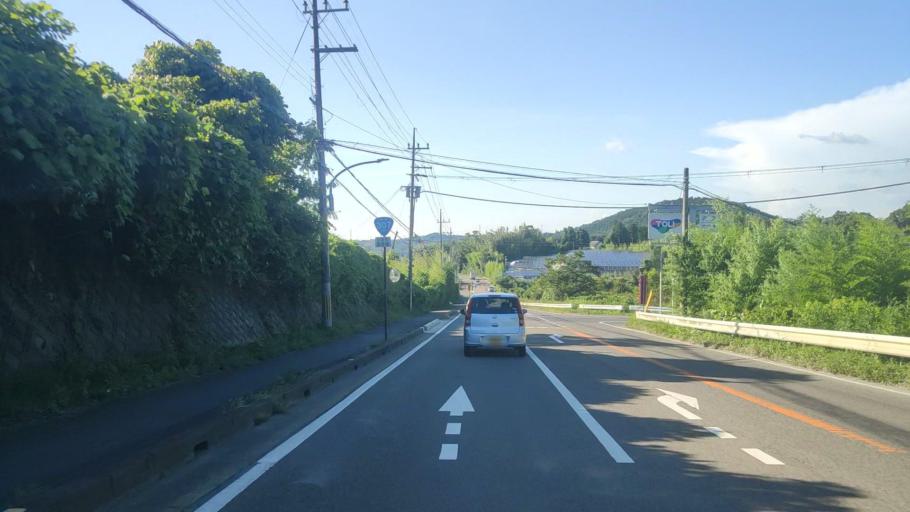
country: JP
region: Shiga Prefecture
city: Hino
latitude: 35.0391
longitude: 136.2432
